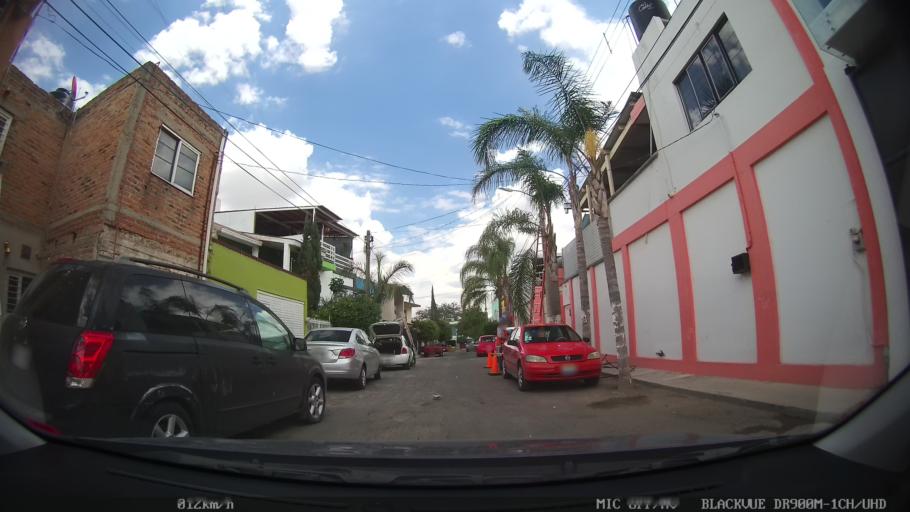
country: MX
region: Jalisco
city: Tlaquepaque
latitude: 20.6359
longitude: -103.2703
